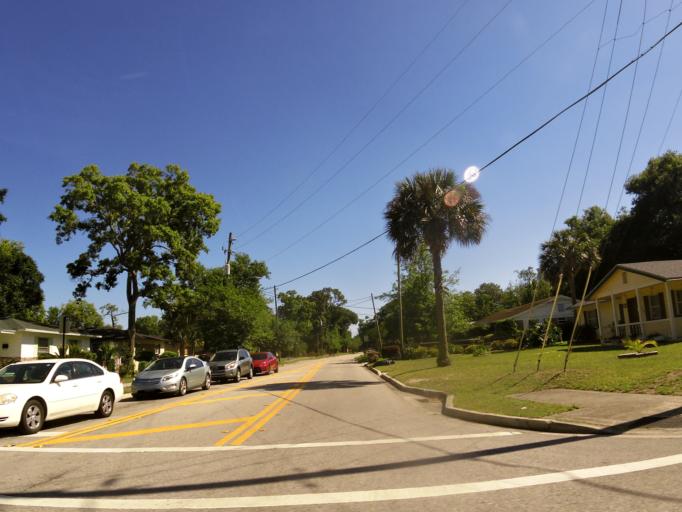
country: US
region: Florida
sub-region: Duval County
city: Jacksonville
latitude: 30.3376
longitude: -81.5741
